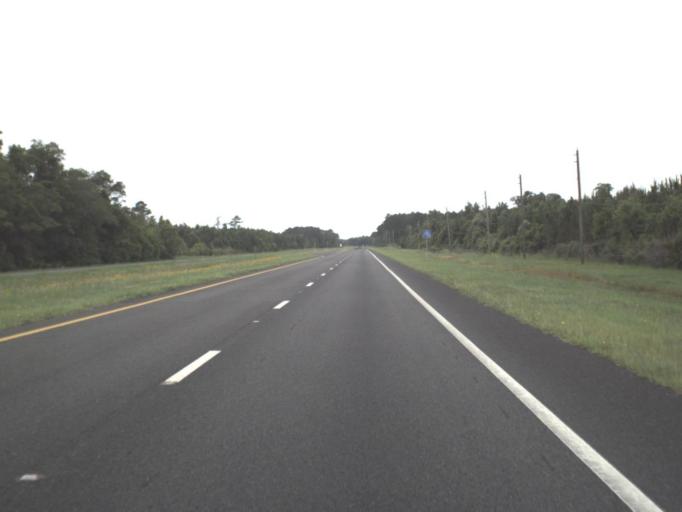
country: US
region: Florida
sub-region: Nassau County
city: Yulee
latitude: 30.6141
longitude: -81.6904
